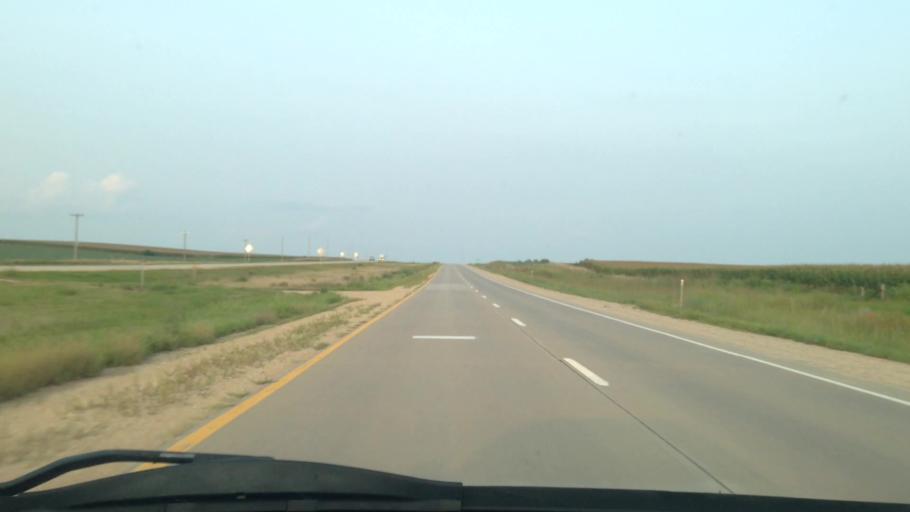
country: US
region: Iowa
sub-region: Benton County
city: Atkins
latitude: 41.9632
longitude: -91.9797
